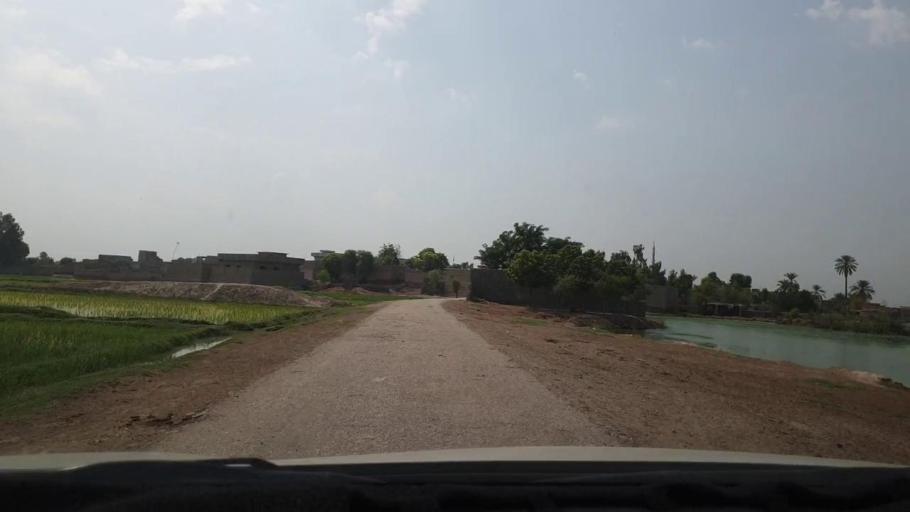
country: PK
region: Sindh
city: Dokri
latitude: 27.3801
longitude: 68.1266
